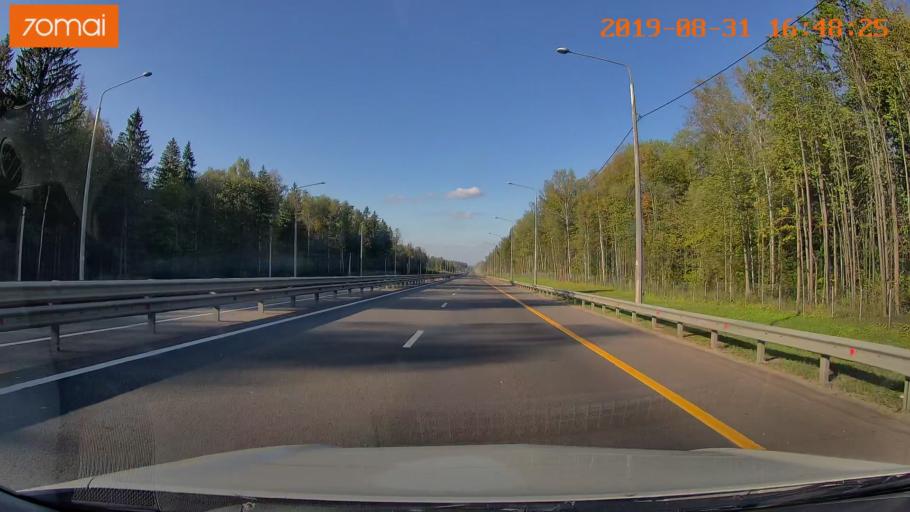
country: RU
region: Kaluga
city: Pyatovskiy
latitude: 54.6718
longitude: 36.1466
